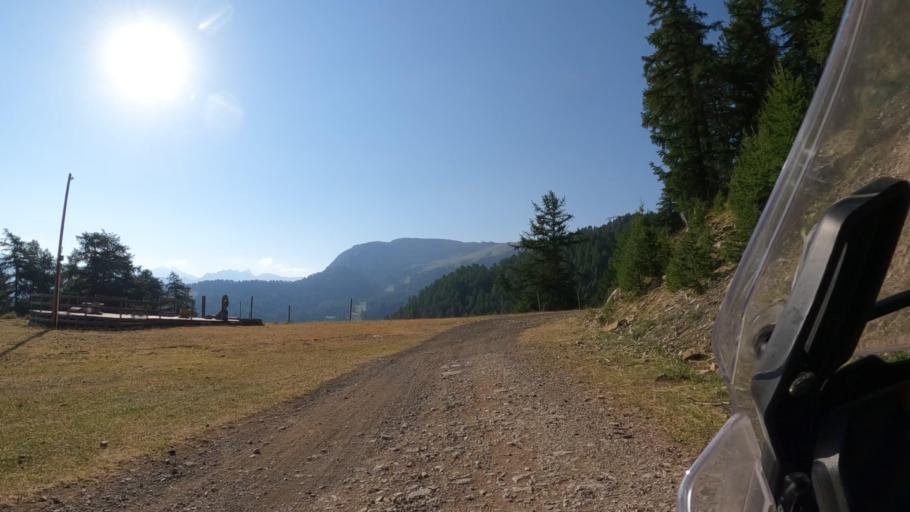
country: FR
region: Provence-Alpes-Cote d'Azur
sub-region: Departement des Hautes-Alpes
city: Guillestre
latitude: 44.6122
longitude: 6.6243
